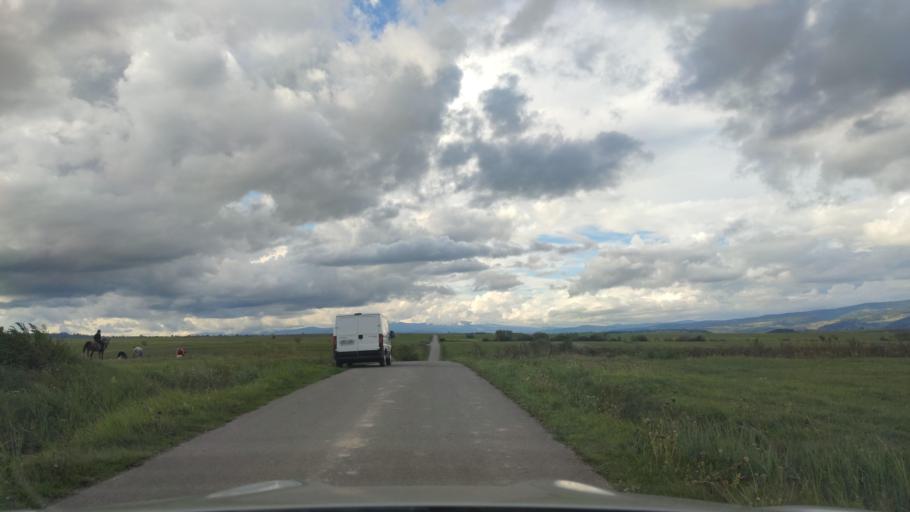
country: RO
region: Harghita
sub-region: Comuna Subcetate
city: Subcetate
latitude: 46.8185
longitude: 25.4328
